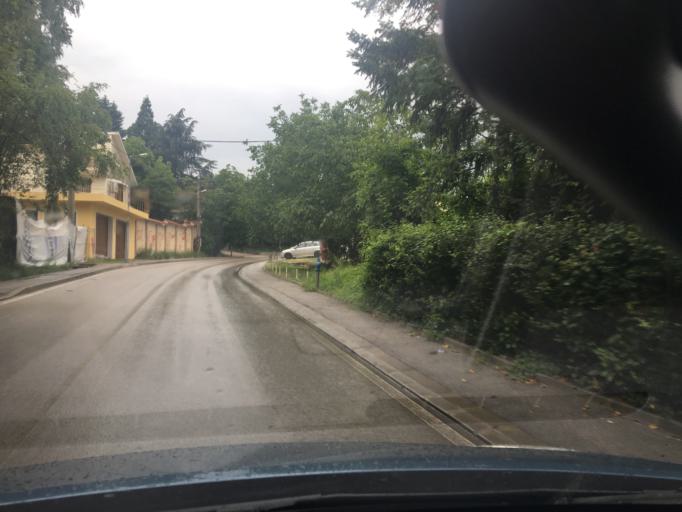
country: BG
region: Sofia-Capital
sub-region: Stolichna Obshtina
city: Sofia
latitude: 42.6434
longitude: 23.2806
